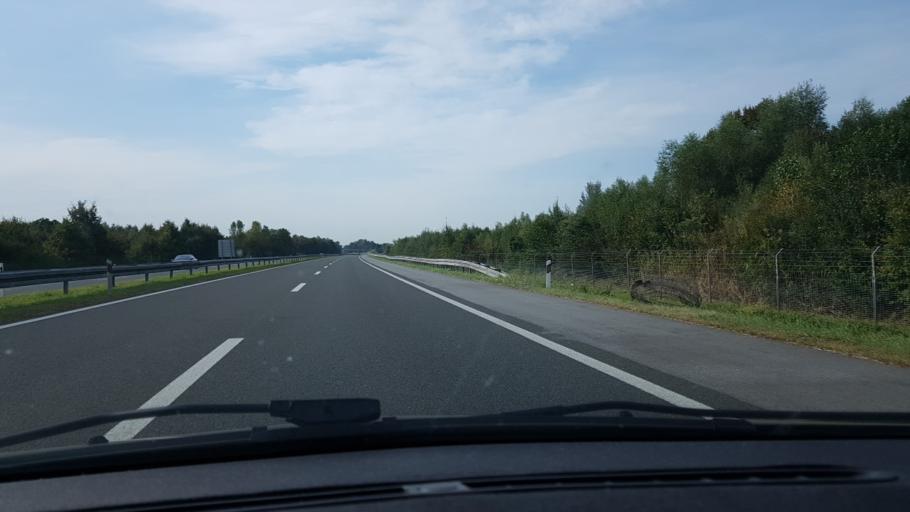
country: HR
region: Zagrebacka
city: Pojatno
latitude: 45.9224
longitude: 15.8262
